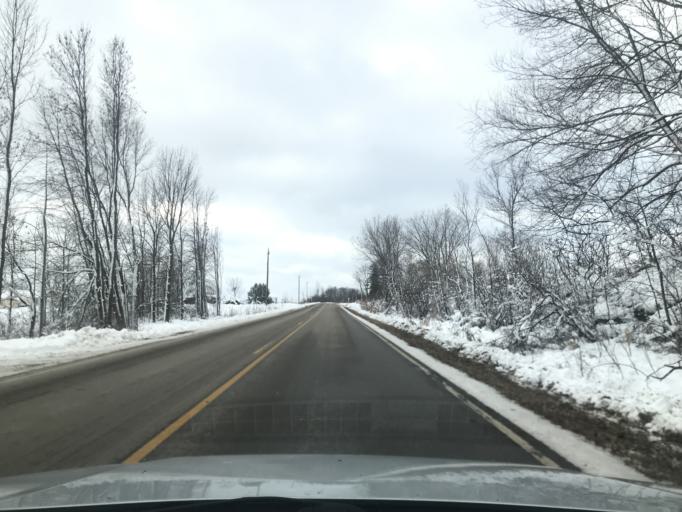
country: US
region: Wisconsin
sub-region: Oconto County
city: Oconto
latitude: 44.9383
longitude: -87.9869
